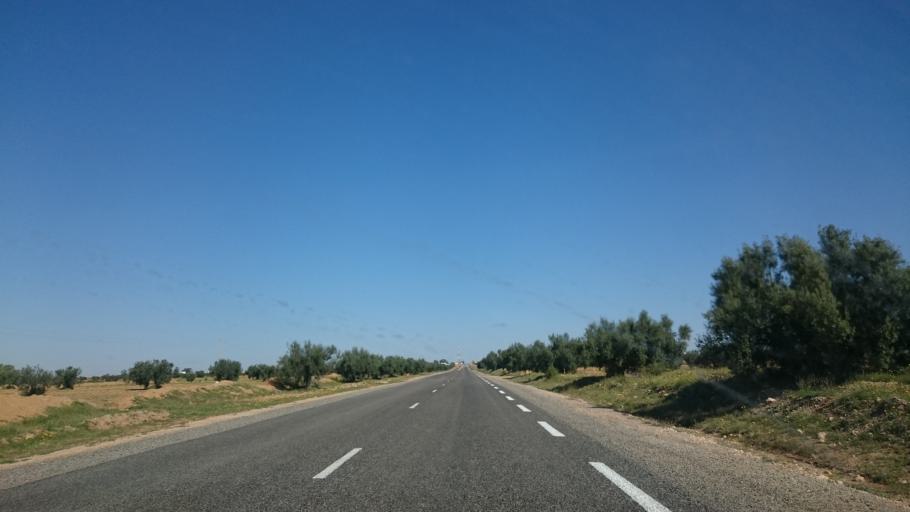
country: TN
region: Safaqis
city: Sfax
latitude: 34.8023
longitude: 10.4854
